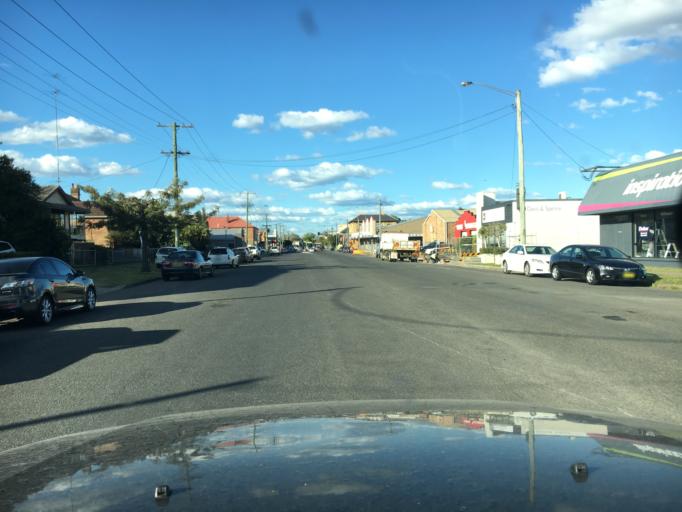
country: AU
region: New South Wales
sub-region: Maitland Municipality
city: East Maitland
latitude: -32.7477
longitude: 151.5798
